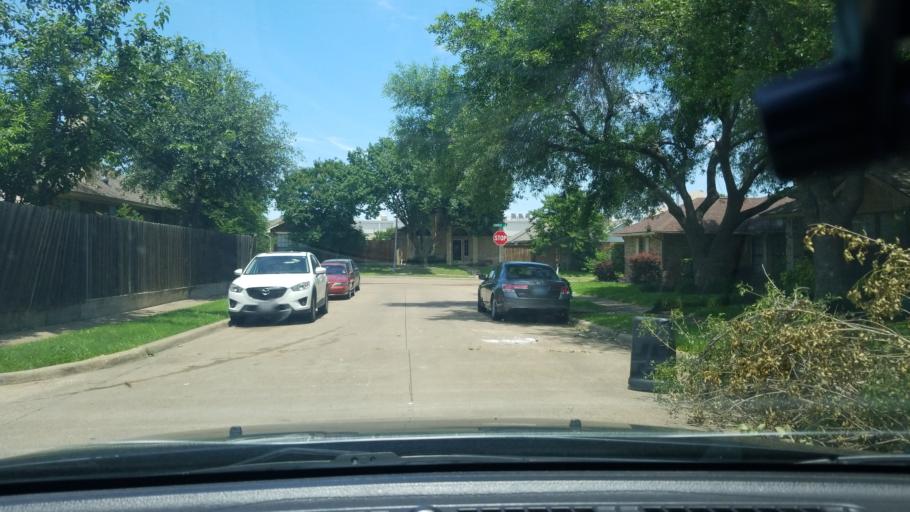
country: US
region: Texas
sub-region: Dallas County
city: Mesquite
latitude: 32.7871
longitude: -96.6000
